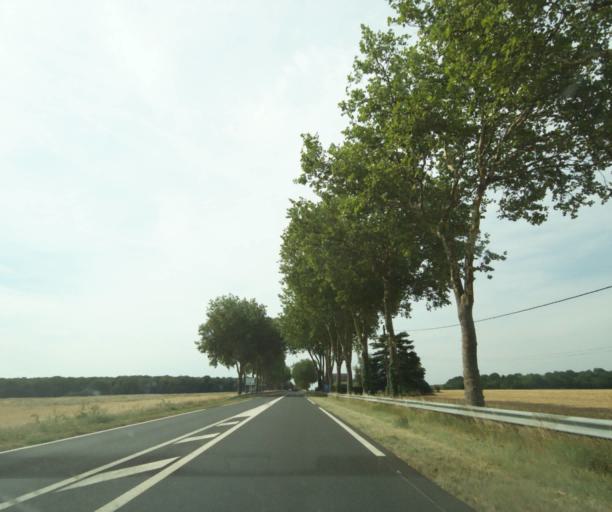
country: FR
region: Centre
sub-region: Departement d'Indre-et-Loire
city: Saint-Antoine-du-Rocher
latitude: 47.5022
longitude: 0.6002
